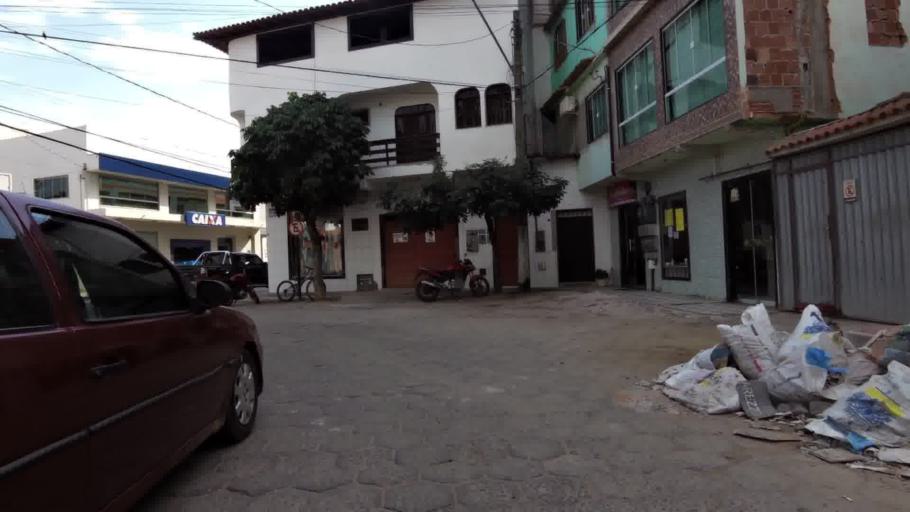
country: BR
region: Espirito Santo
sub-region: Piuma
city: Piuma
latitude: -20.8367
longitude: -40.7268
